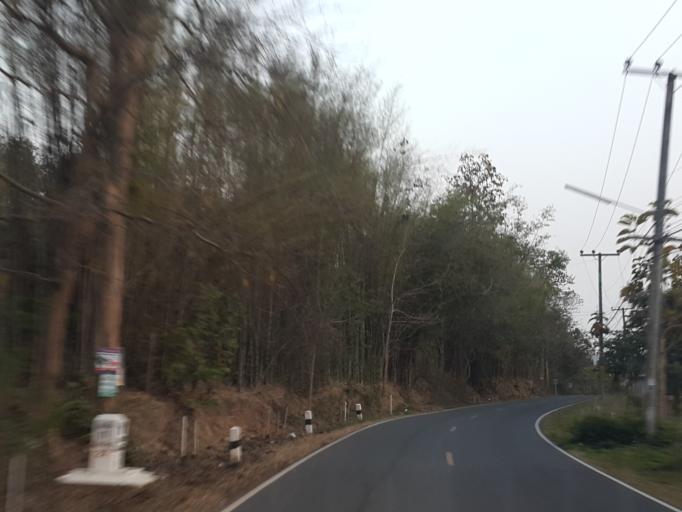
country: TH
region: Chiang Mai
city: Mae Taeng
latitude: 18.9857
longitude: 98.9074
